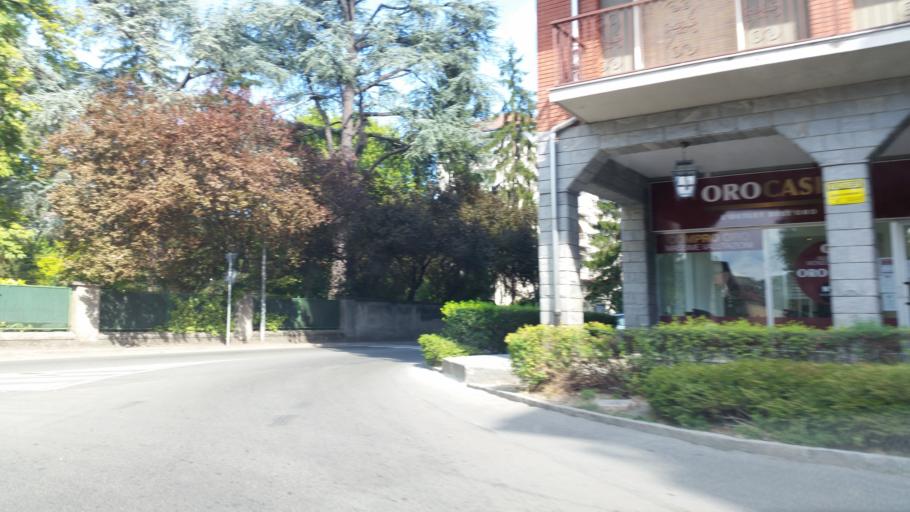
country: IT
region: Piedmont
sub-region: Provincia di Alessandria
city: Acqui Terme
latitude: 44.6751
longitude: 8.4735
